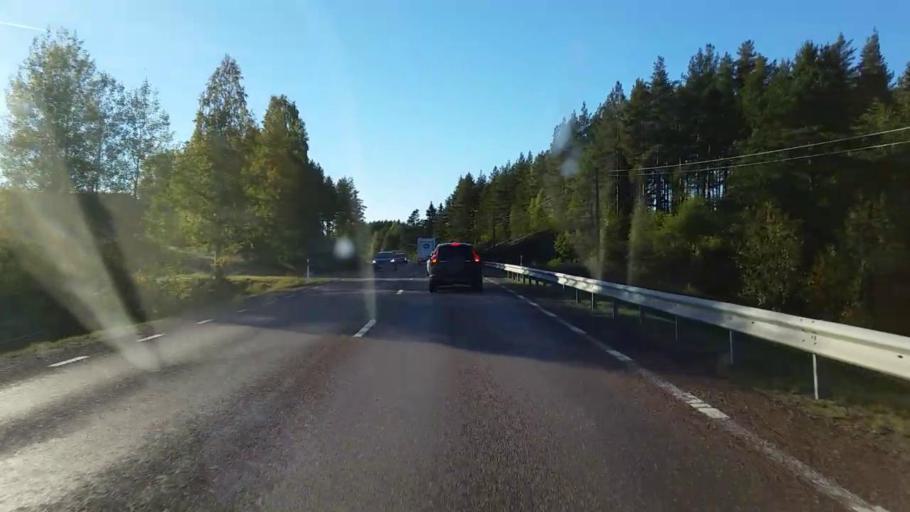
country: SE
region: Gaevleborg
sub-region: Ljusdals Kommun
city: Jaervsoe
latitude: 61.8047
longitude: 16.2910
